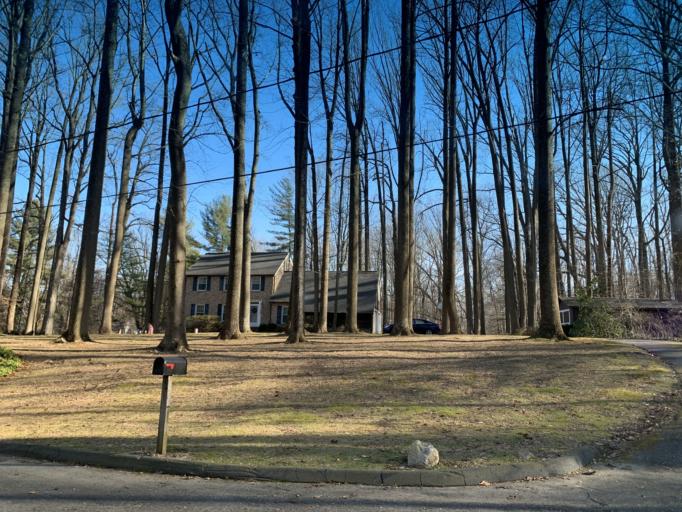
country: US
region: Maryland
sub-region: Harford County
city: Riverside
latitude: 39.5716
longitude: -76.2469
